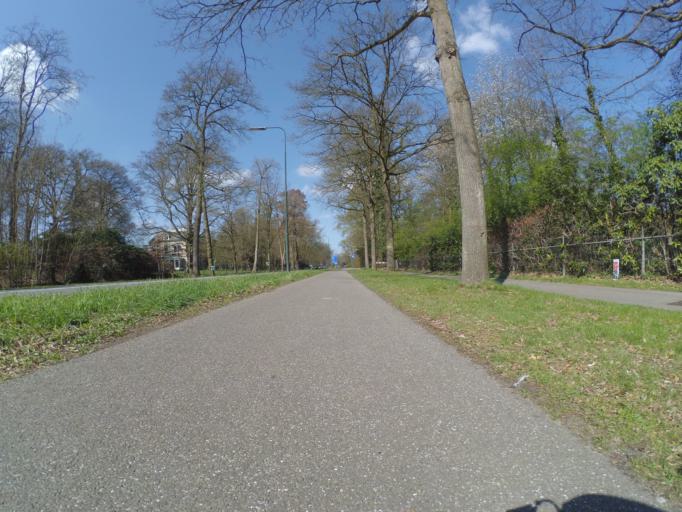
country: NL
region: Utrecht
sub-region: Gemeente Utrechtse Heuvelrug
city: Driebergen-Rijsenburg
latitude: 52.0461
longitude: 5.2988
